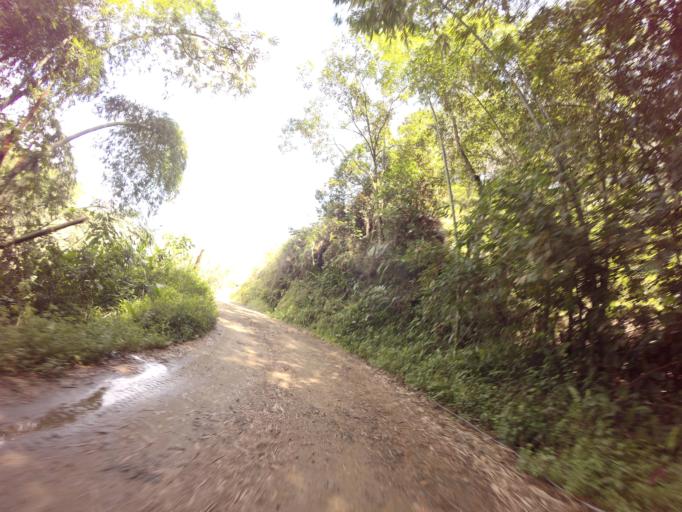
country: CO
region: Caldas
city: Pensilvania
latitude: 5.4923
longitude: -75.1850
